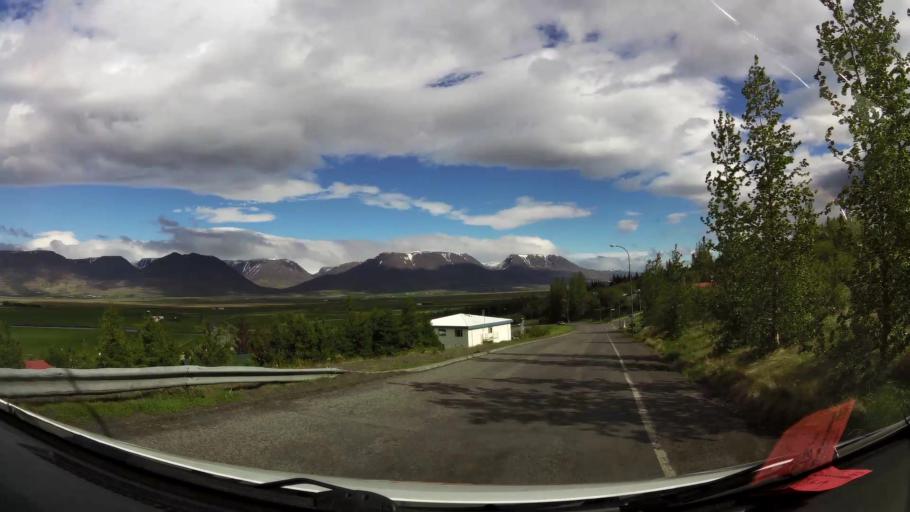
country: IS
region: Northwest
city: Saudarkrokur
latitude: 65.5533
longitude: -19.4495
